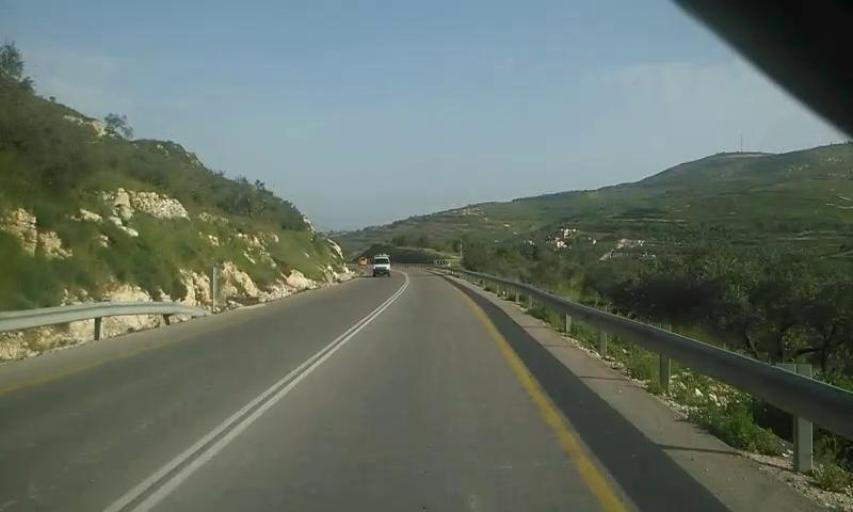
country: PS
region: West Bank
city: Madama
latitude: 32.1859
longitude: 35.2338
